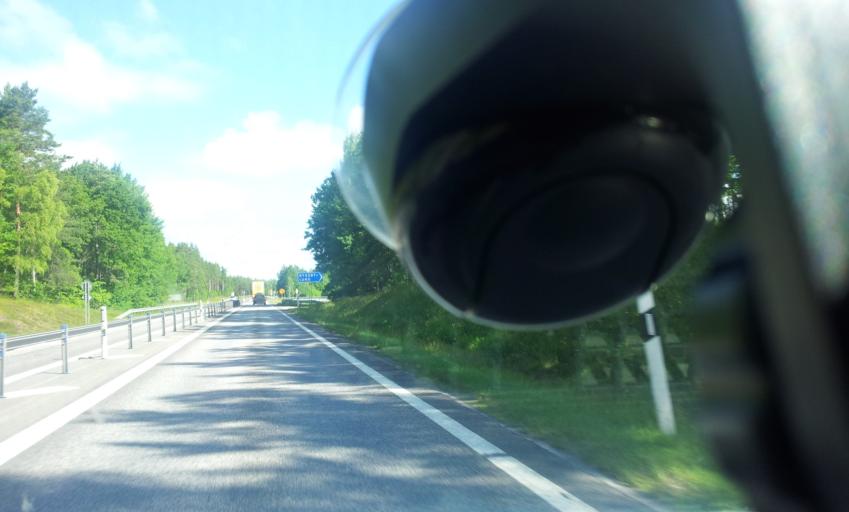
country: SE
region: Kalmar
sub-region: Kalmar Kommun
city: Lindsdal
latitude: 56.8285
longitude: 16.3674
